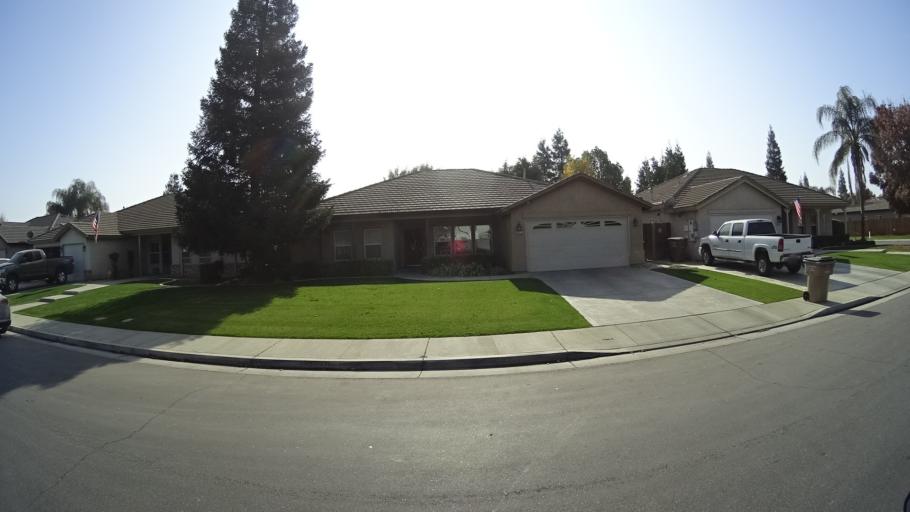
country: US
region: California
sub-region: Kern County
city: Greenacres
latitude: 35.4256
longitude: -119.1129
